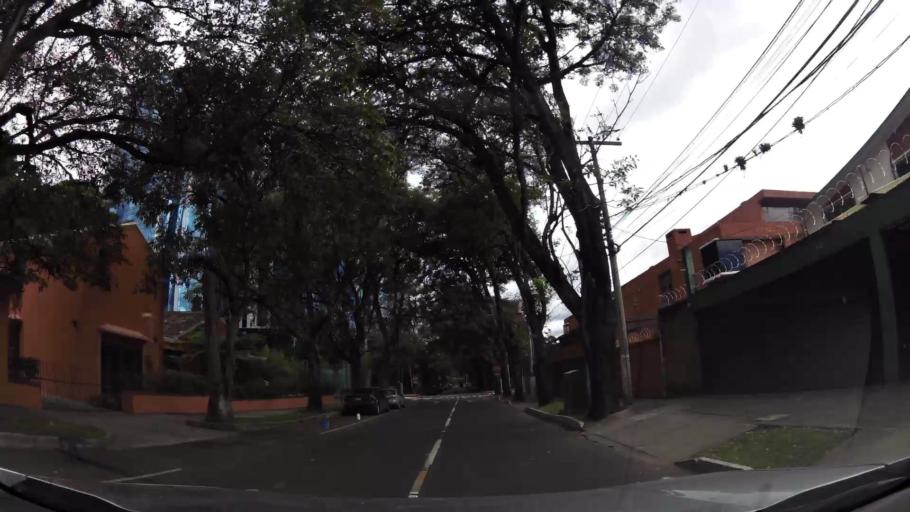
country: GT
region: Guatemala
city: Santa Catarina Pinula
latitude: 14.6016
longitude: -90.5113
